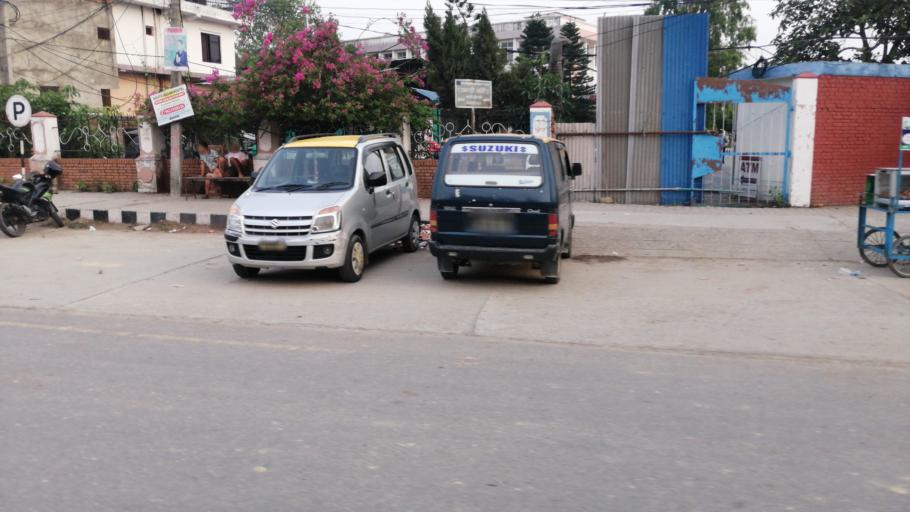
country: NP
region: Western Region
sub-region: Lumbini Zone
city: Bhairahawa
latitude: 27.4903
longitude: 83.4490
